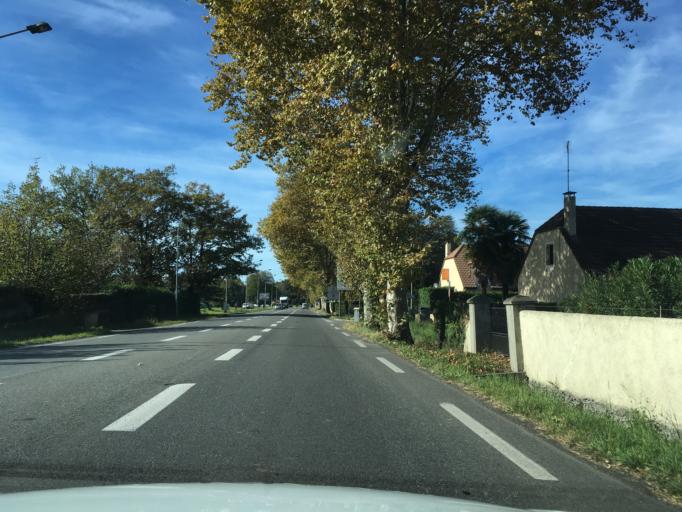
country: FR
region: Aquitaine
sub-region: Departement des Pyrenees-Atlantiques
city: Pau
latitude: 43.3289
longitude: -0.3516
